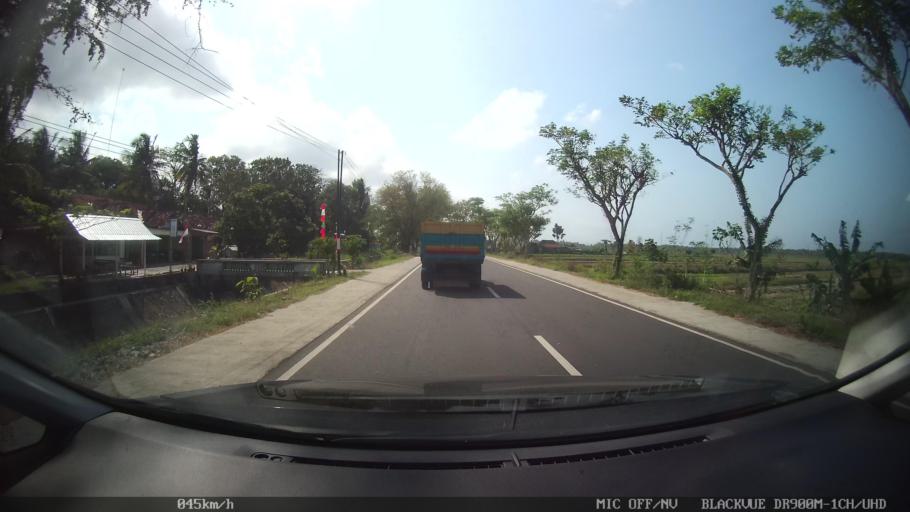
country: ID
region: Daerah Istimewa Yogyakarta
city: Srandakan
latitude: -7.8965
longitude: 110.1575
